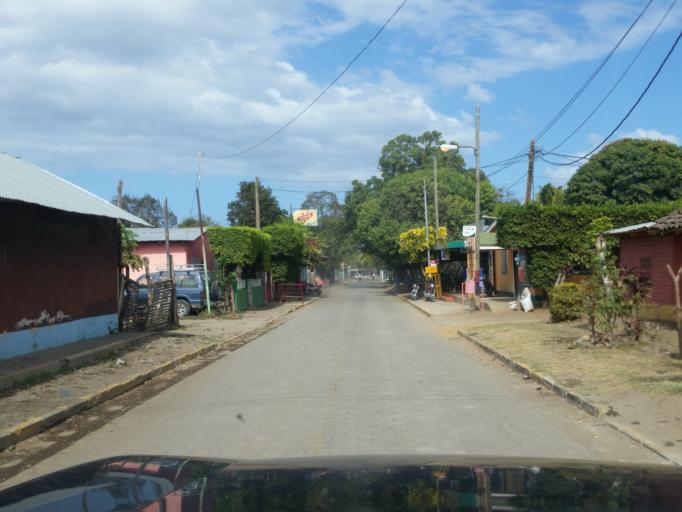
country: NI
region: Rivas
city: Potosi
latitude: 11.4927
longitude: -85.8560
